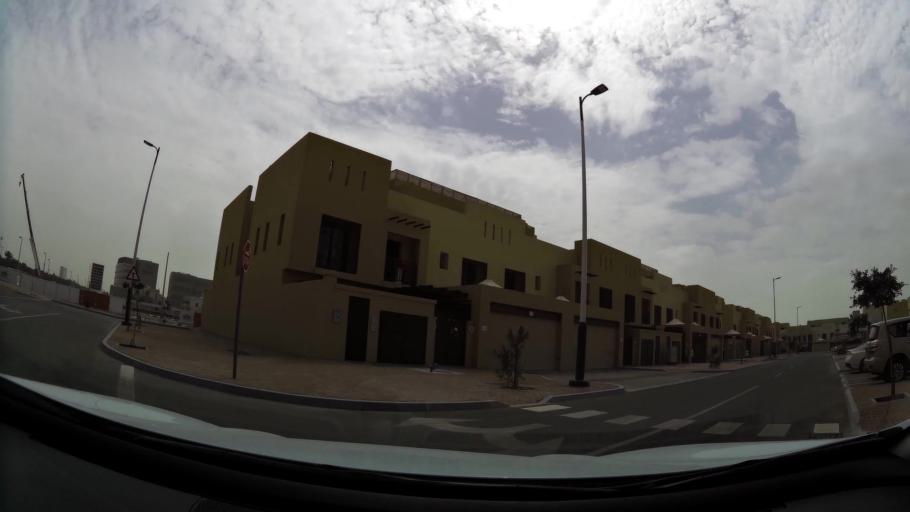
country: AE
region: Abu Dhabi
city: Abu Dhabi
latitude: 24.3979
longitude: 54.4969
